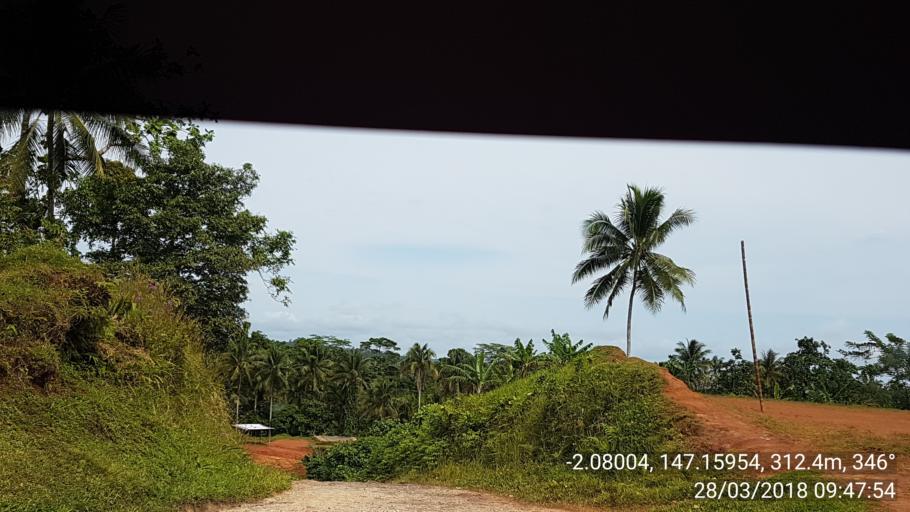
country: PG
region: Manus
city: Lorengau
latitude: -2.0800
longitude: 147.1594
